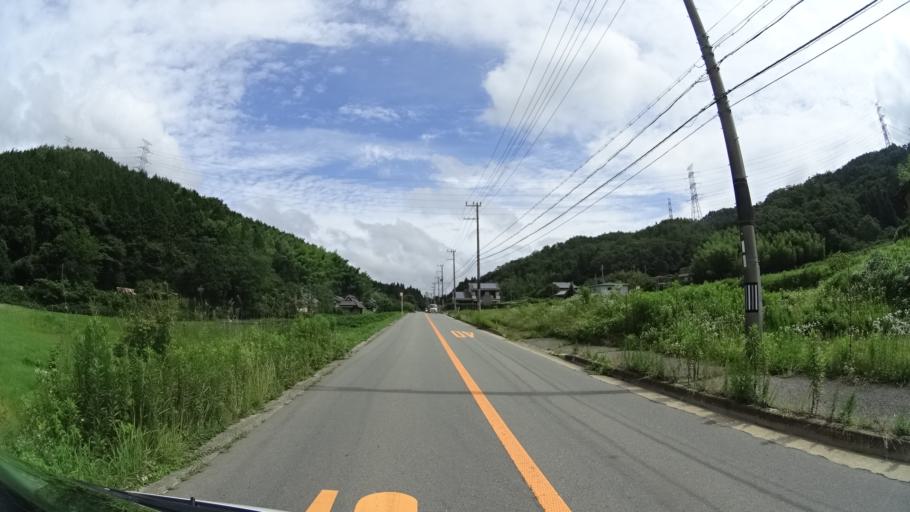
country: JP
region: Kyoto
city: Kameoka
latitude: 34.9902
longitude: 135.4764
